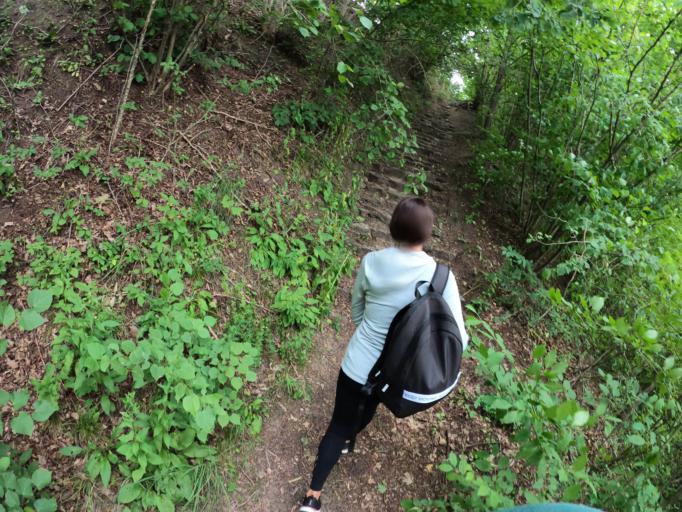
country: LT
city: Jieznas
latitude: 54.5120
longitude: 24.0890
